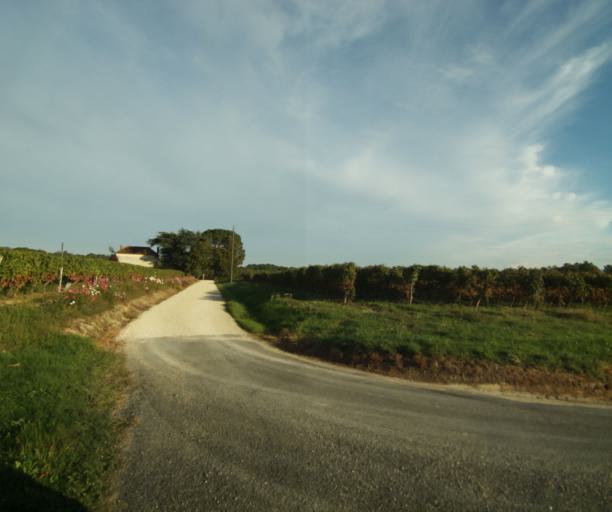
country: FR
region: Midi-Pyrenees
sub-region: Departement du Gers
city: Cazaubon
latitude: 43.8709
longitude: 0.0024
